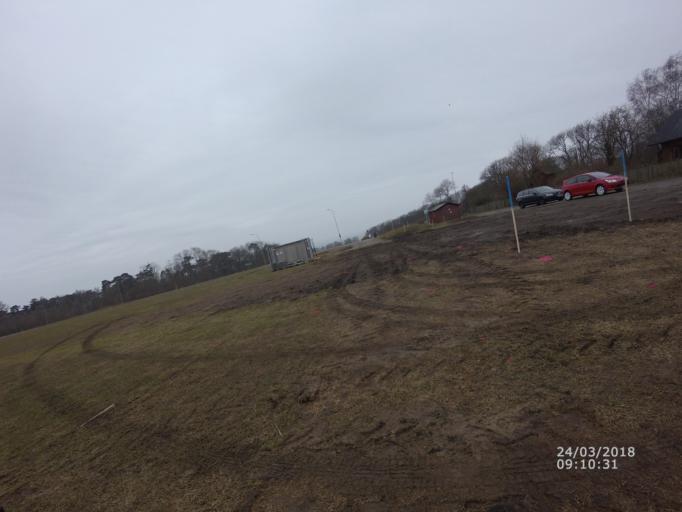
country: SE
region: Skane
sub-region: Helsingborg
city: Helsingborg
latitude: 56.0827
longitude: 12.6643
